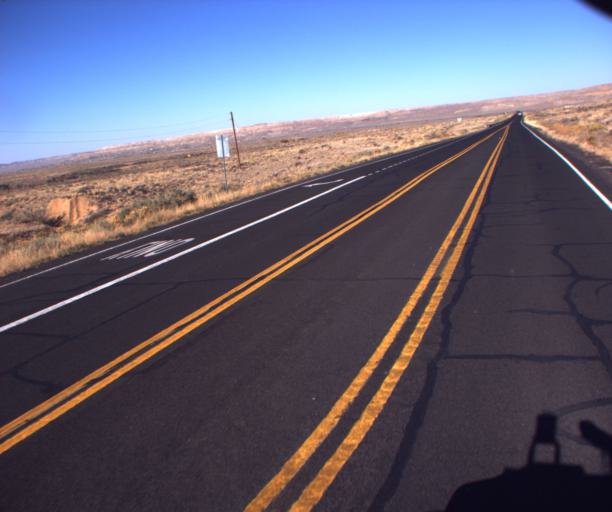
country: US
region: Arizona
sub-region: Navajo County
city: First Mesa
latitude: 35.8332
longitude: -110.2957
